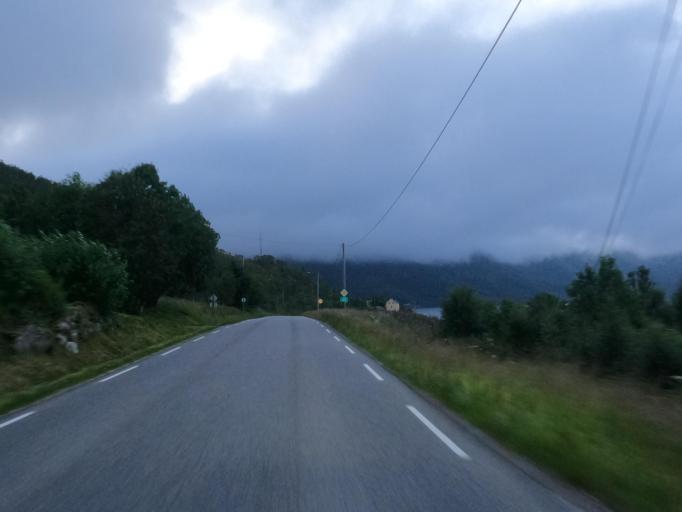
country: NO
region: Nordland
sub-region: Lodingen
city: Lodingen
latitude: 68.6060
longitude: 15.7788
